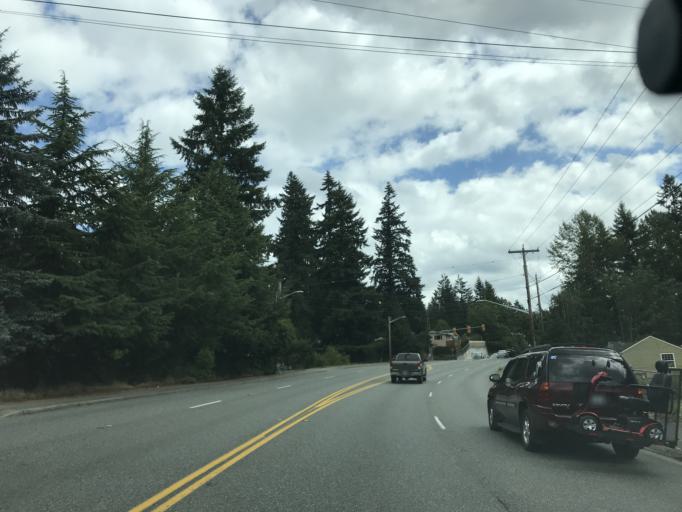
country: US
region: Washington
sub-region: King County
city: Fairwood
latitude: 47.4462
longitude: -122.1720
